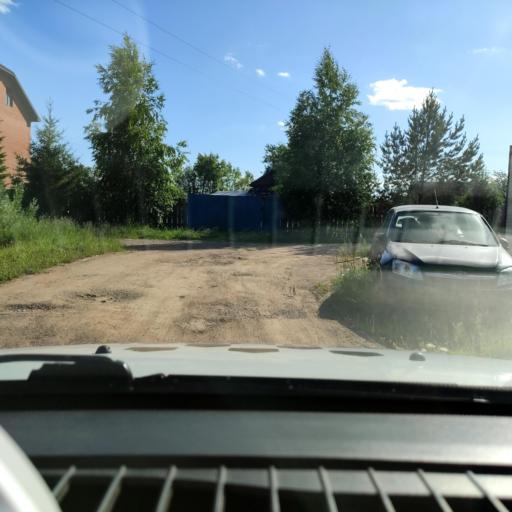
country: RU
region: Perm
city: Froly
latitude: 57.9195
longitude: 56.2629
